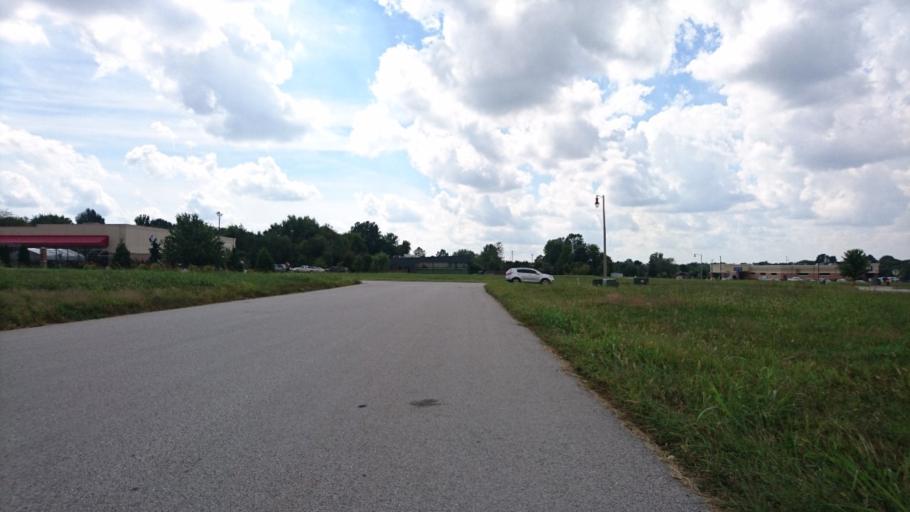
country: US
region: Missouri
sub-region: Greene County
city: Springfield
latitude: 37.2097
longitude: -93.3465
